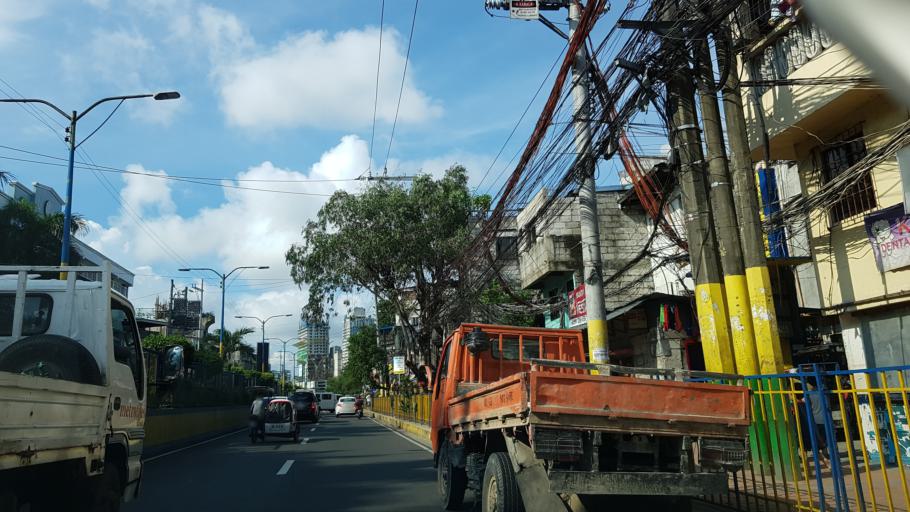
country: PH
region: Metro Manila
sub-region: Mandaluyong
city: Mandaluyong City
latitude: 14.5832
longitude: 121.0371
